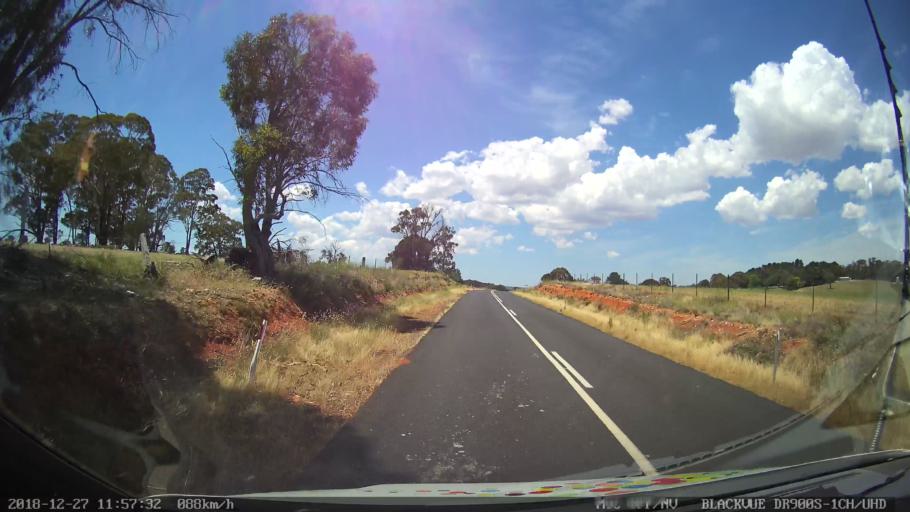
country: AU
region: New South Wales
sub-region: Blayney
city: Blayney
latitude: -33.7128
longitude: 149.3875
